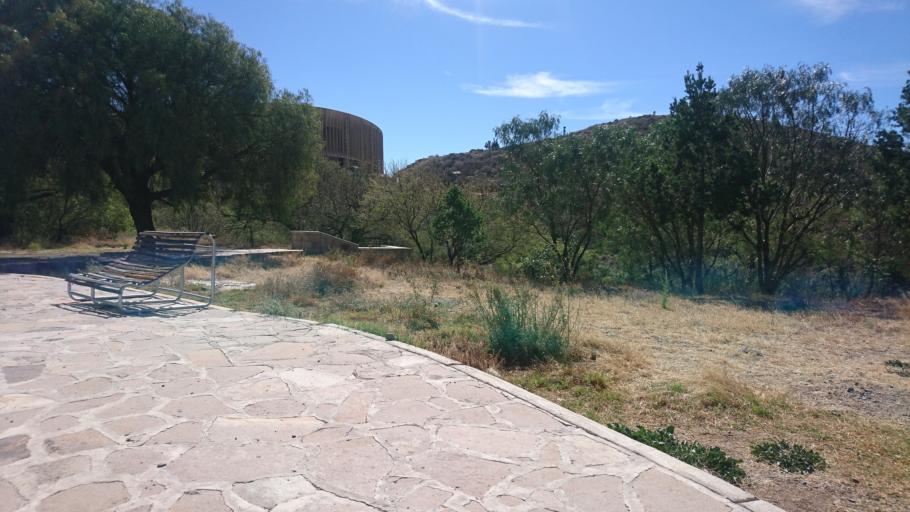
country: MX
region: Zacatecas
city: Guadalupe
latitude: 22.7801
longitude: -102.5444
